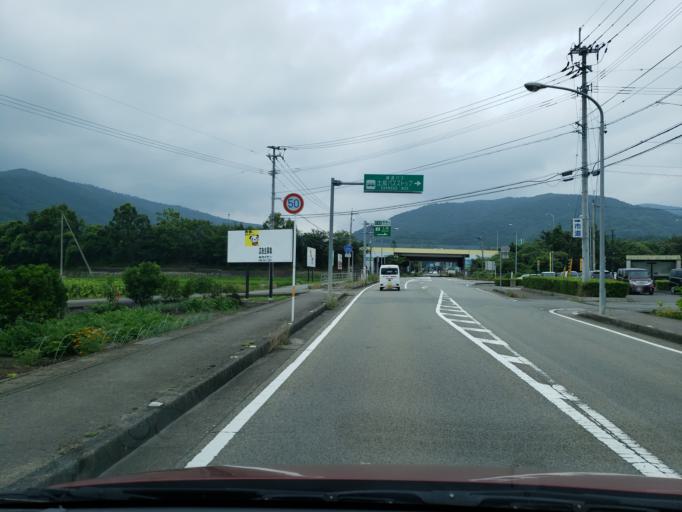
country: JP
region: Tokushima
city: Kamojimacho-jogejima
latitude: 34.1193
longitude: 134.3533
